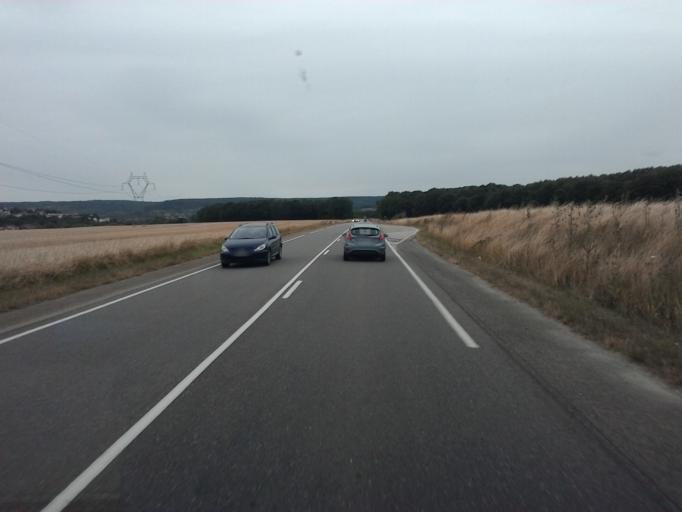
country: FR
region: Lorraine
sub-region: Departement de Meurthe-et-Moselle
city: Bainville-sur-Madon
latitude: 48.5867
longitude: 6.1096
